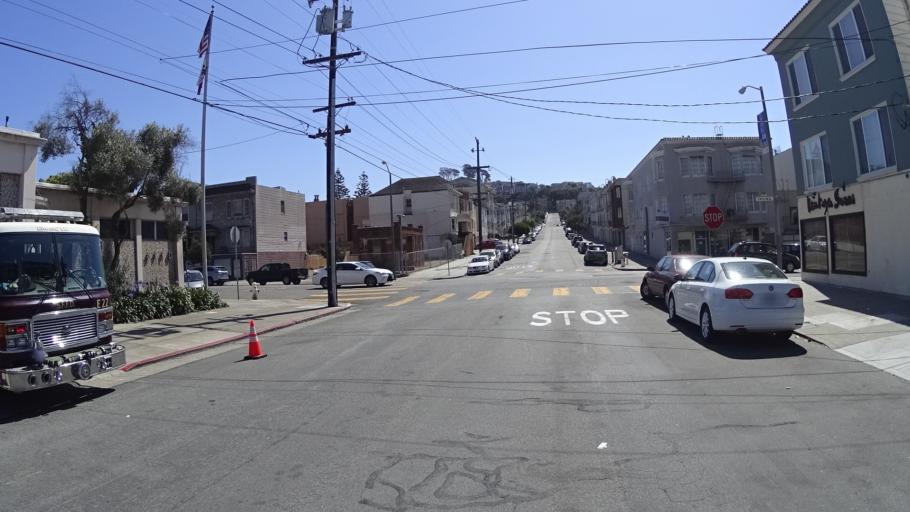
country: US
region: California
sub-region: San Francisco County
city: San Francisco
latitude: 37.7641
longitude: -122.4739
